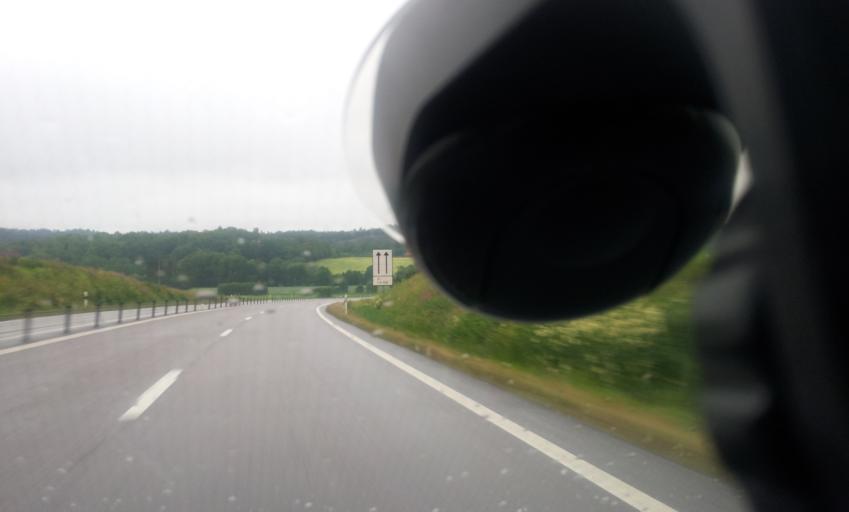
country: SE
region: Kalmar
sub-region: Vasterviks Kommun
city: Forserum
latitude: 58.0047
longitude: 16.4893
